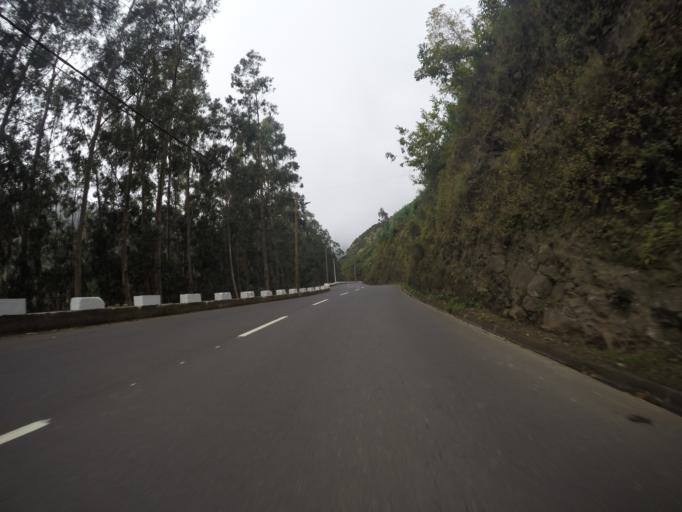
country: PT
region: Madeira
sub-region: Camara de Lobos
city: Curral das Freiras
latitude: 32.6999
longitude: -16.9531
